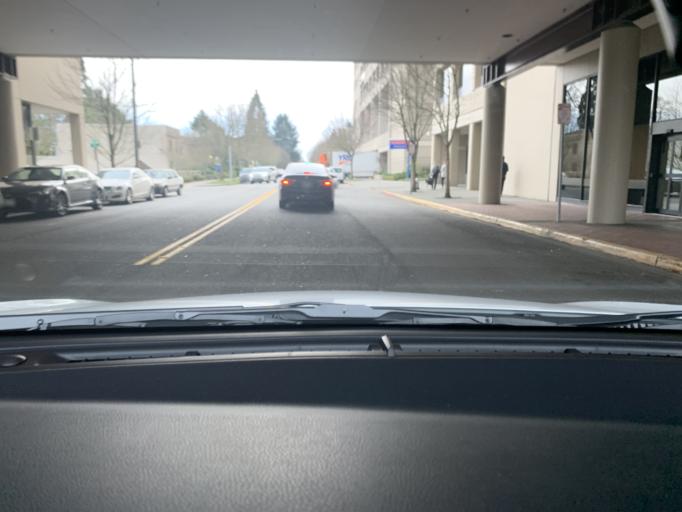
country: US
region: Washington
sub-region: Pierce County
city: Tacoma
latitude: 47.2599
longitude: -122.4520
